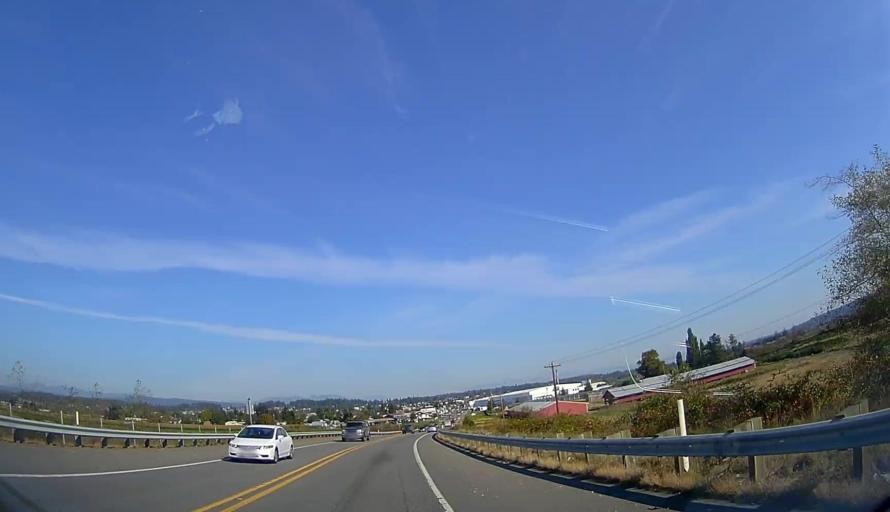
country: US
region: Washington
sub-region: Snohomish County
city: Stanwood
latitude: 48.2408
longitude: -122.3810
